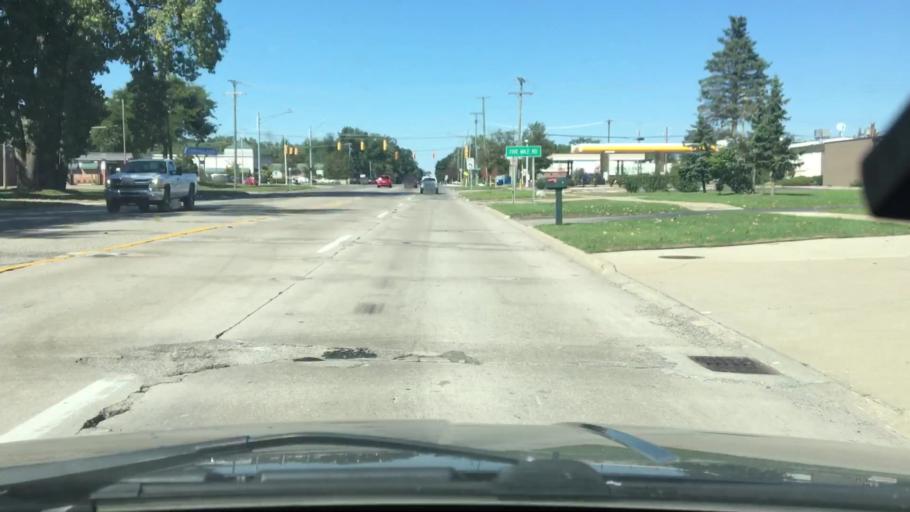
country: US
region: Michigan
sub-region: Wayne County
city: Livonia
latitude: 42.3964
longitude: -83.3539
